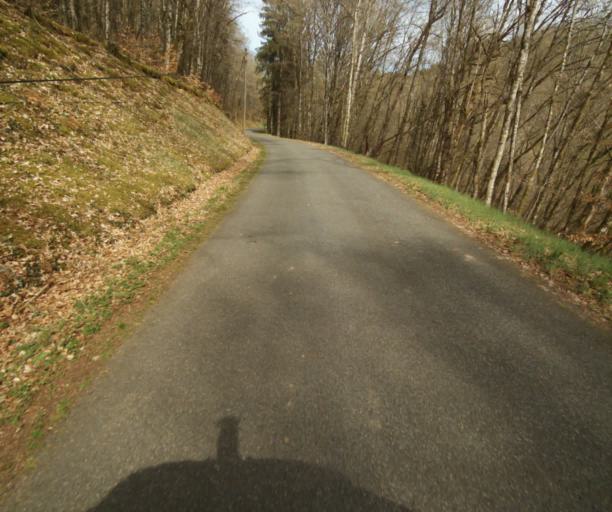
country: FR
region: Limousin
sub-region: Departement de la Correze
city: Naves
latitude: 45.3514
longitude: 1.8154
